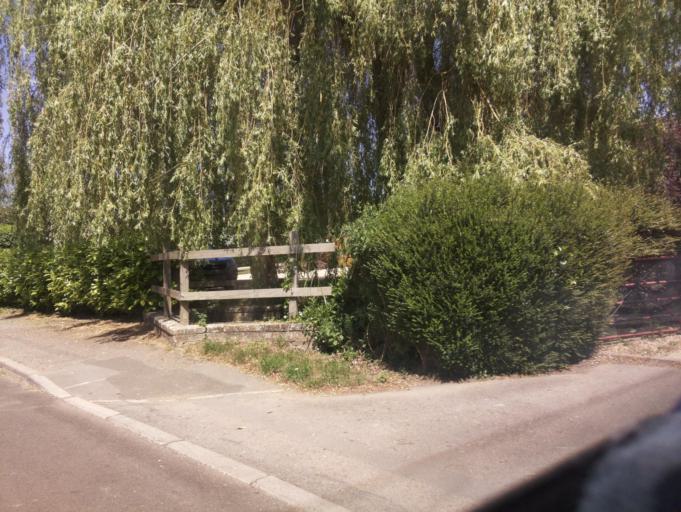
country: GB
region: England
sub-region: Wiltshire
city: Bremhill
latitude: 51.5088
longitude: -2.0530
